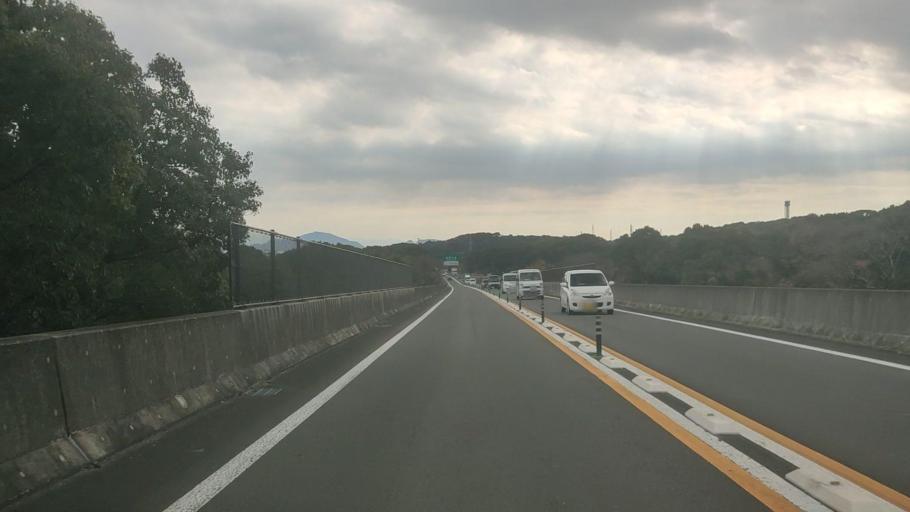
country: JP
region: Nagasaki
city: Shimabara
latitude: 32.7690
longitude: 130.3586
